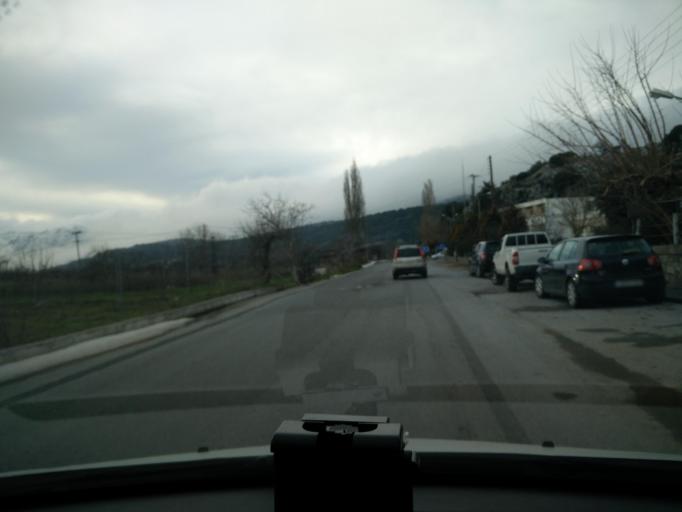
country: GR
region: Crete
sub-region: Nomos Irakleiou
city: Malia
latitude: 35.2011
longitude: 25.4826
